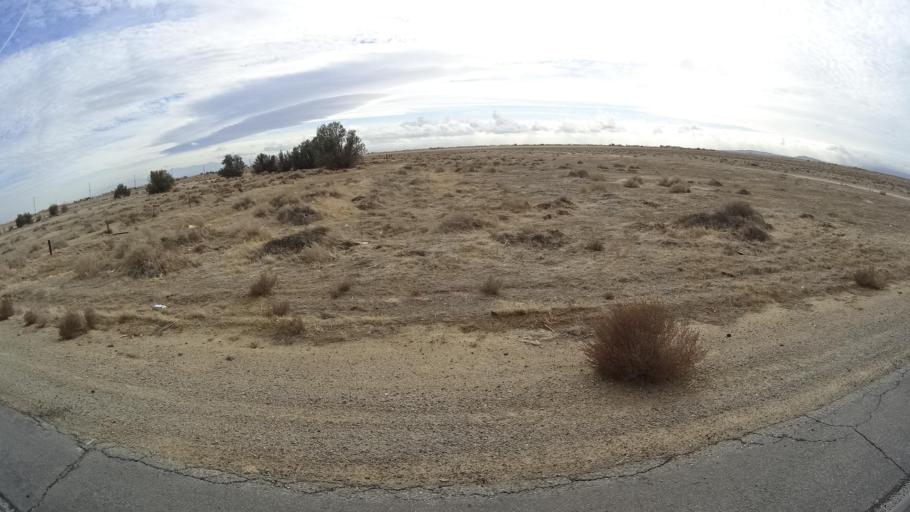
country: US
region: California
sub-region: Kern County
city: Rosamond
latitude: 34.8637
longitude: -118.2594
